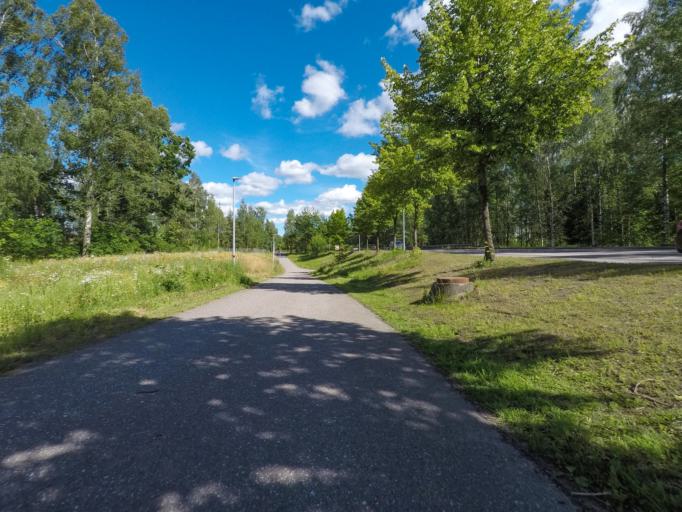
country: FI
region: South Karelia
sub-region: Lappeenranta
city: Lappeenranta
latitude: 61.0607
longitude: 28.2405
